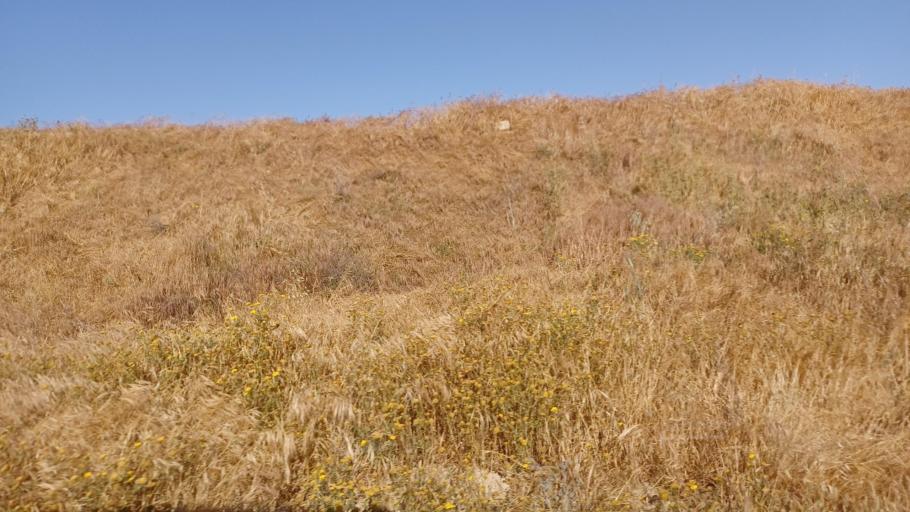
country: CY
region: Lefkosia
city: Mammari
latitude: 35.1579
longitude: 33.2432
